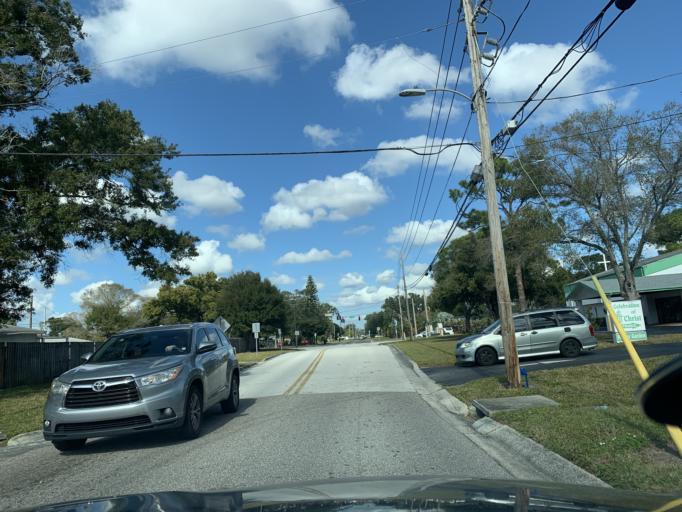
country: US
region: Florida
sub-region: Pinellas County
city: Kenneth City
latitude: 27.8054
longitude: -82.7369
